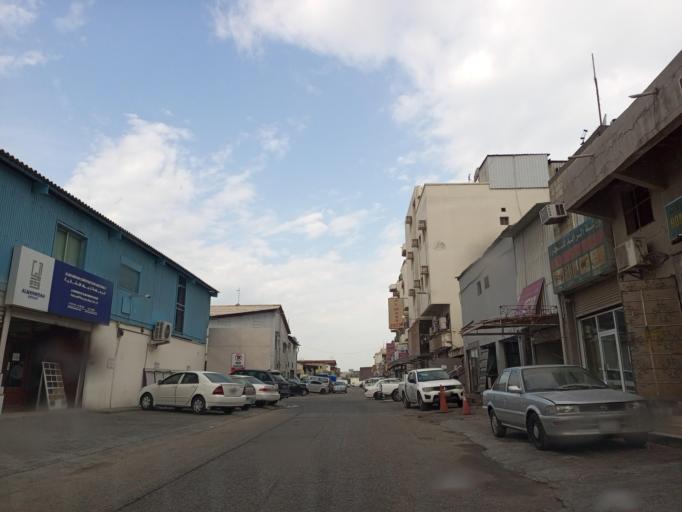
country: BH
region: Muharraq
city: Al Hadd
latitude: 26.2591
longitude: 50.6444
